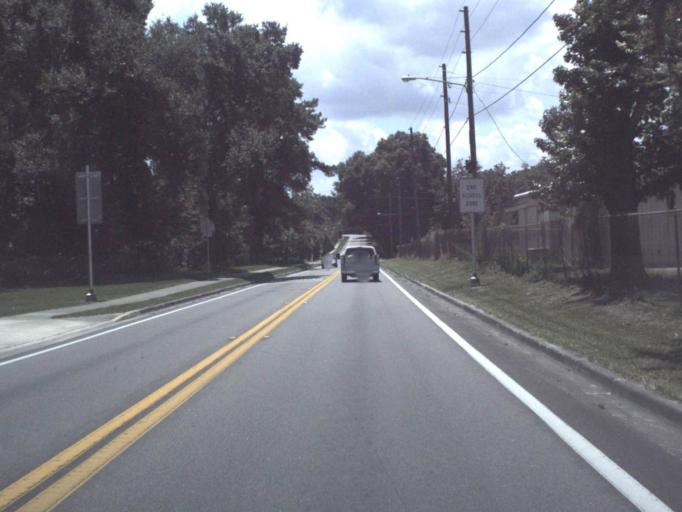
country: US
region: Florida
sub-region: Alachua County
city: Archer
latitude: 29.5280
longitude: -82.5192
